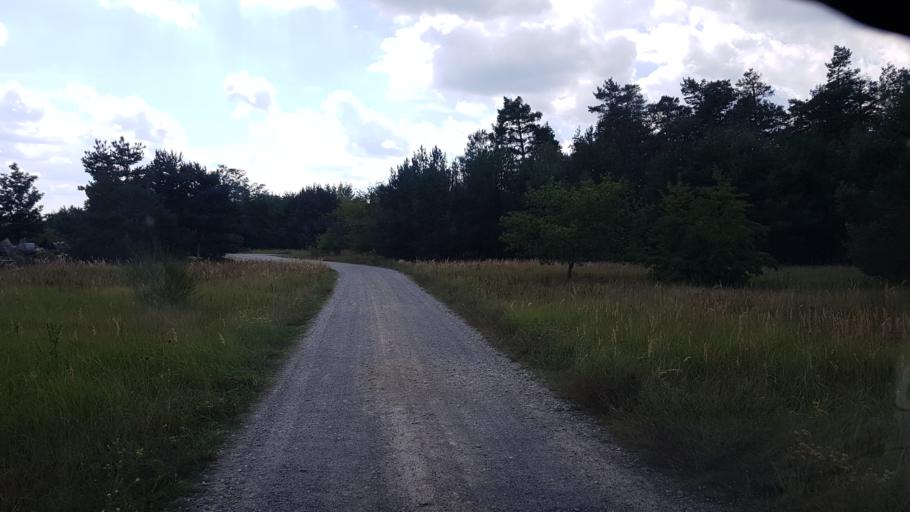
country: DE
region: Brandenburg
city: Lubbenau
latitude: 51.8068
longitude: 13.8898
